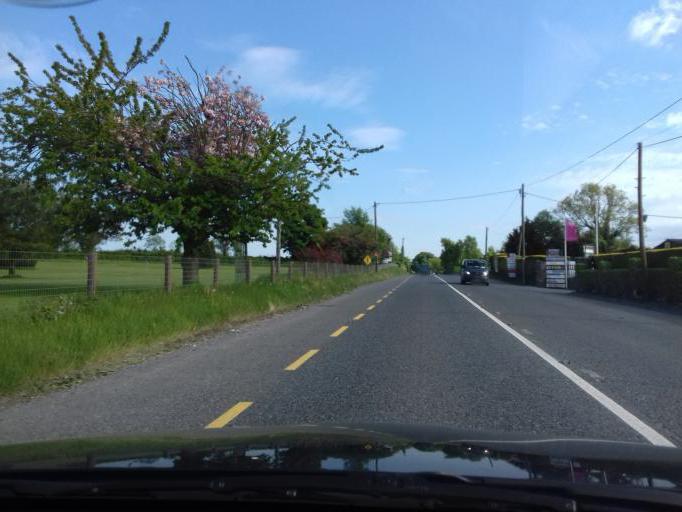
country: IE
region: Leinster
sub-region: Dublin City
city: Finglas
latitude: 53.4321
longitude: -6.3323
